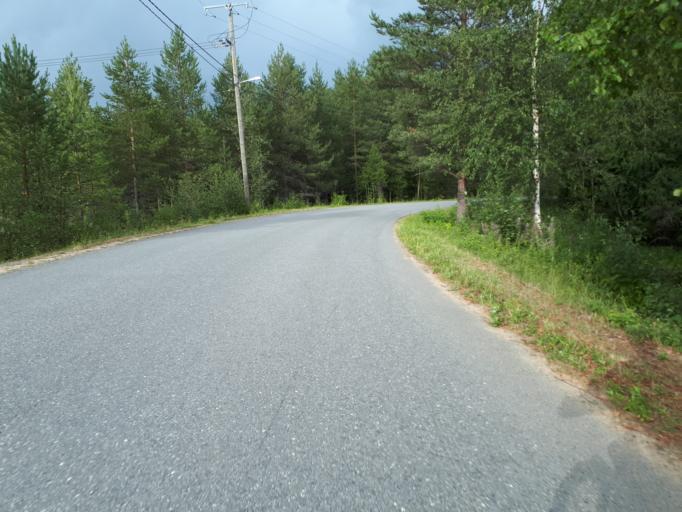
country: FI
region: Northern Ostrobothnia
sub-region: Oulunkaari
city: Ii
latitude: 65.3328
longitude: 25.3865
